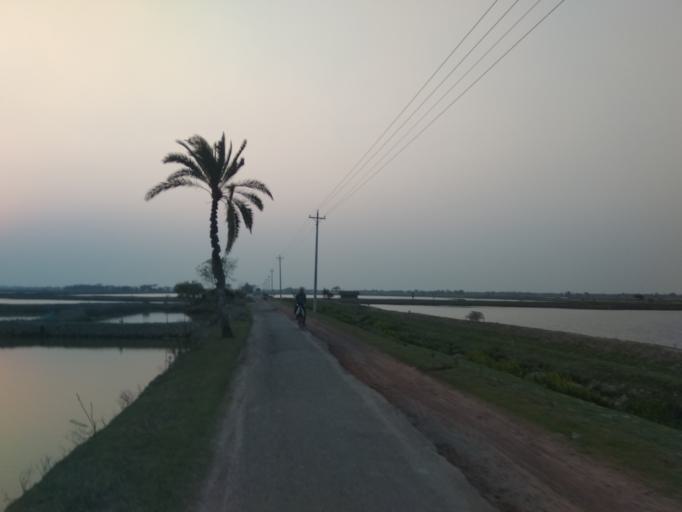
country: IN
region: West Bengal
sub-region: North 24 Parganas
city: Taki
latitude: 22.4571
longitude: 89.0720
